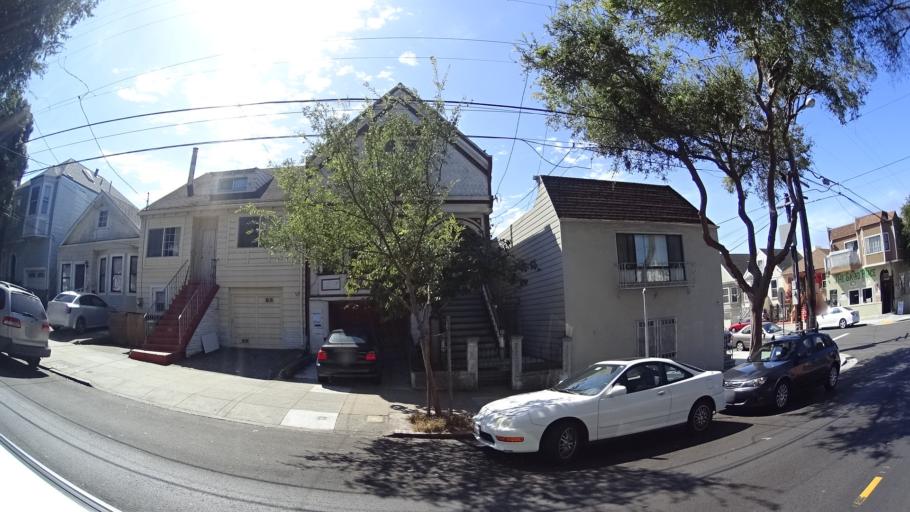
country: US
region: California
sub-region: San Mateo County
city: Daly City
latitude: 37.7227
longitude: -122.4349
